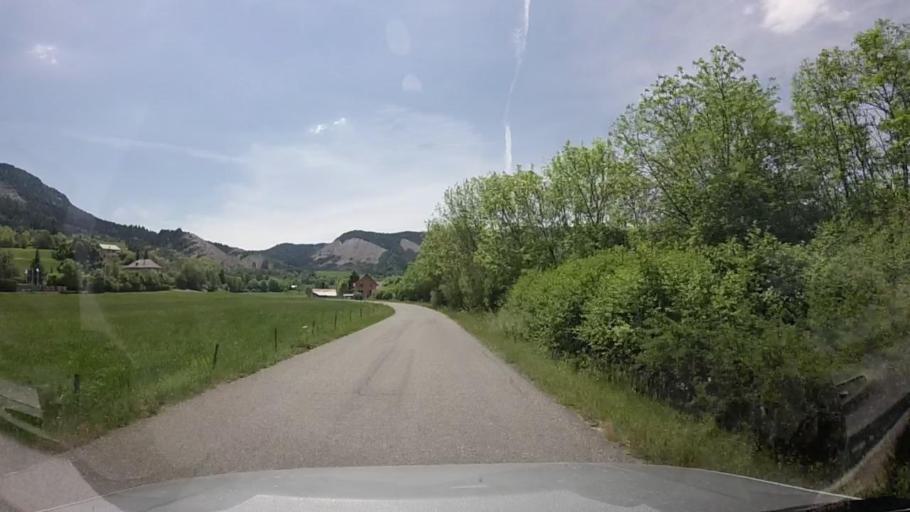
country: FR
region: Provence-Alpes-Cote d'Azur
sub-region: Departement des Alpes-de-Haute-Provence
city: Seyne-les-Alpes
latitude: 44.3438
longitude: 6.3587
